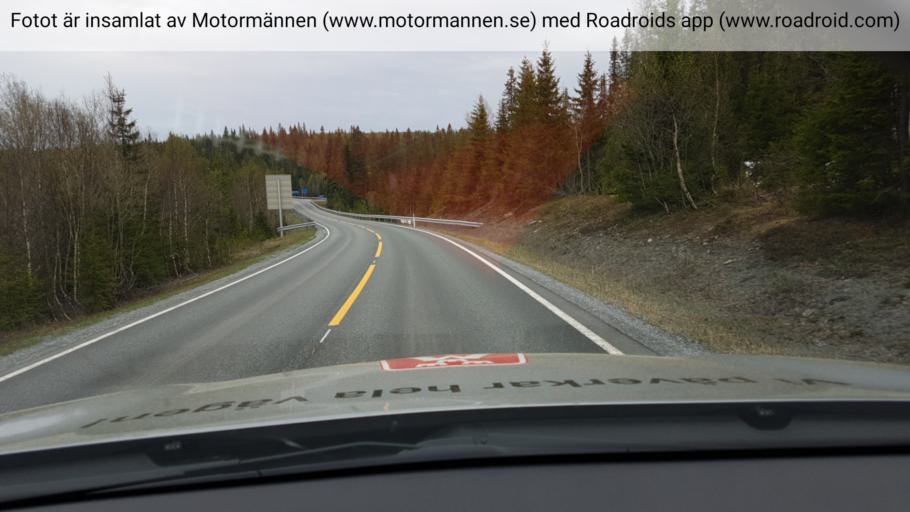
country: NO
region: Nord-Trondelag
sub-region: Meraker
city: Meraker
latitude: 63.6509
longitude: 12.2515
